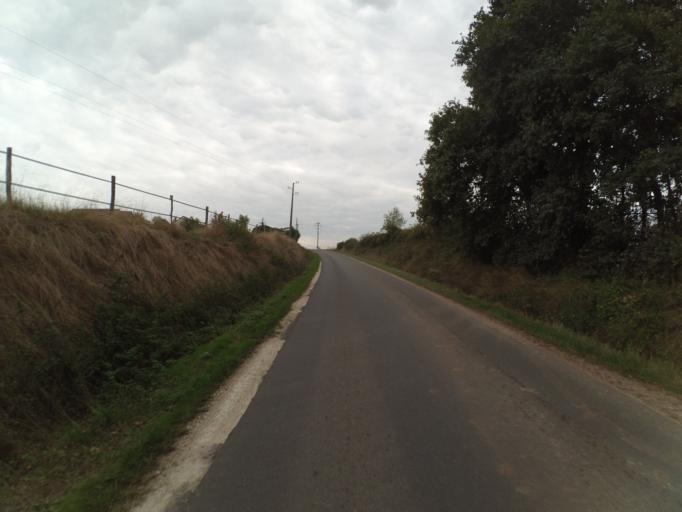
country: FR
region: Centre
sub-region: Departement d'Indre-et-Loire
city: Auzouer-en-Touraine
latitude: 47.4980
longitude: 0.9297
